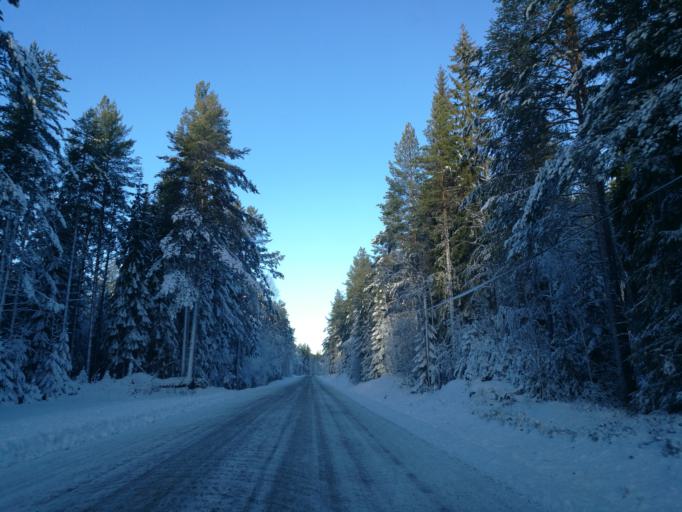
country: NO
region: Hedmark
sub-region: Grue
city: Kirkenaer
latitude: 60.4969
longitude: 12.5623
